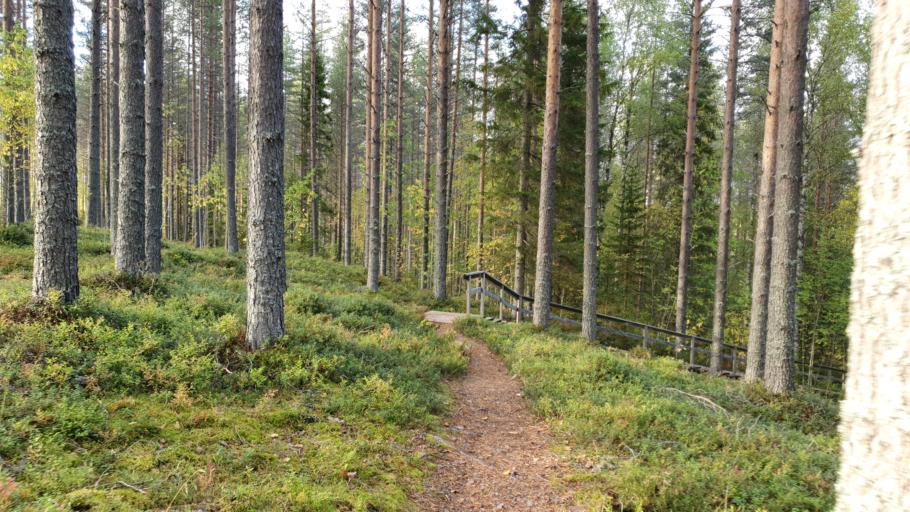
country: FI
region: Kainuu
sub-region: Kehys-Kainuu
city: Kuhmo
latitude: 63.9324
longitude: 29.9701
